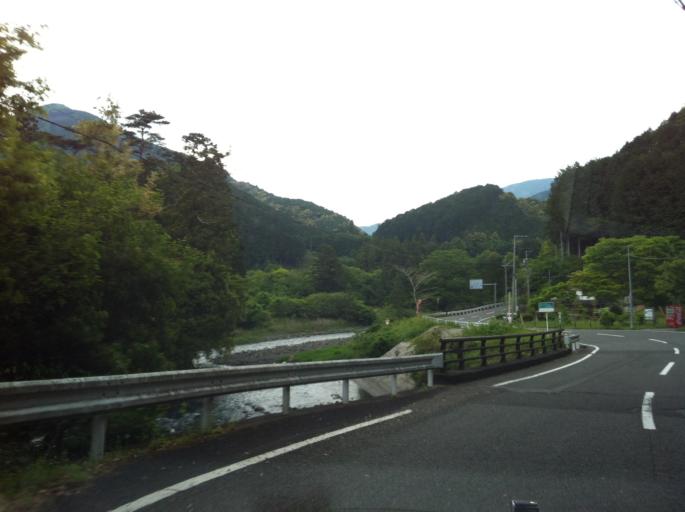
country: JP
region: Shizuoka
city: Shizuoka-shi
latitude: 35.1420
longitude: 138.3297
